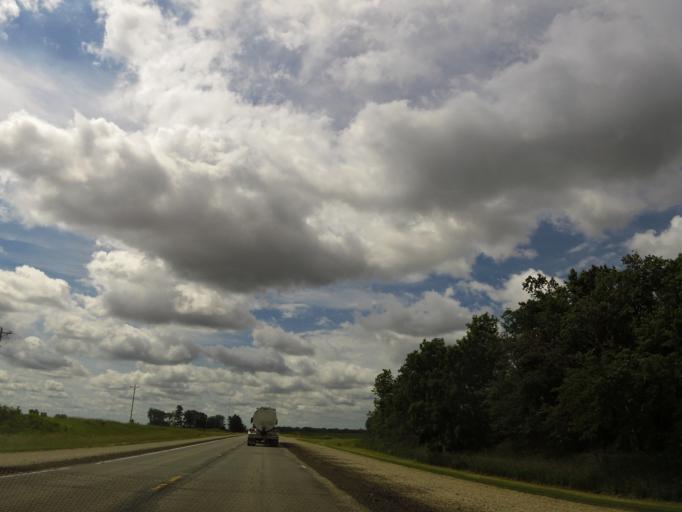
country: US
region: Iowa
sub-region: Howard County
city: Cresco
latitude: 43.2961
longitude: -92.2988
